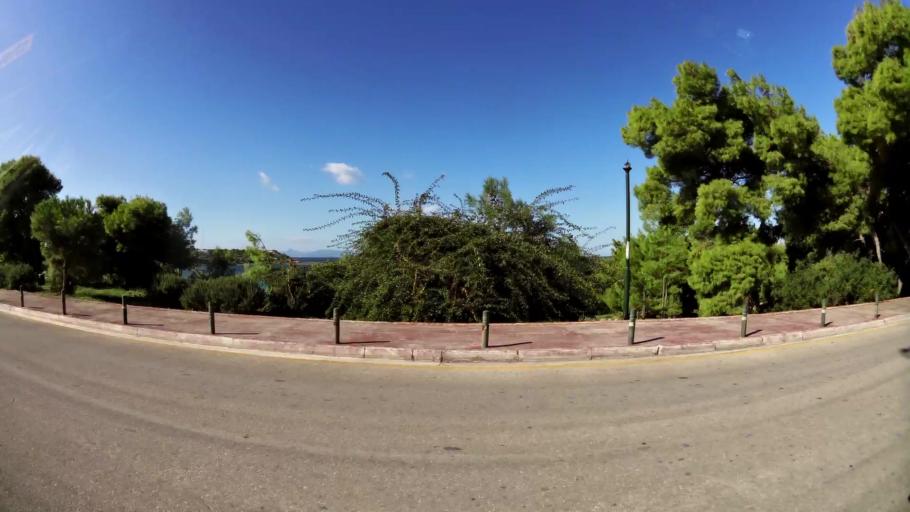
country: GR
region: Attica
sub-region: Nomarchia Anatolikis Attikis
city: Vouliagmeni
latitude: 37.8218
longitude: 23.7703
